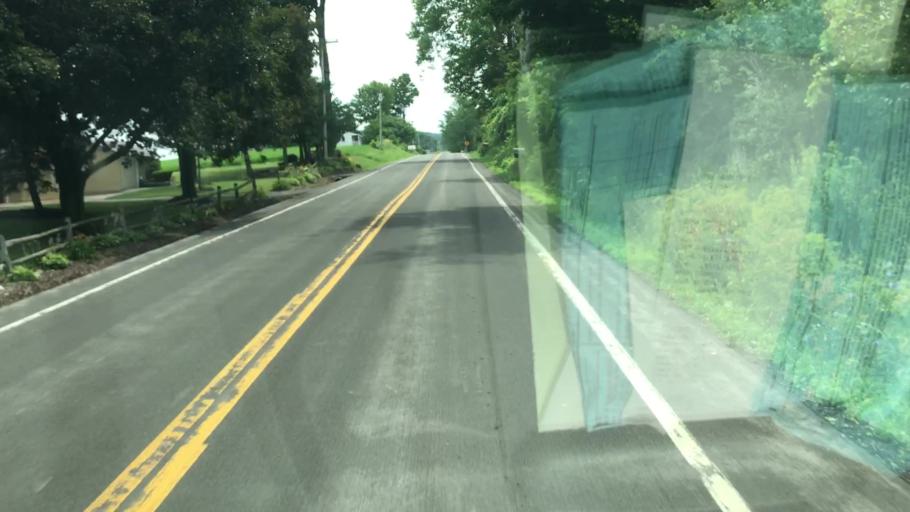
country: US
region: New York
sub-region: Onondaga County
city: Manlius
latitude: 42.9317
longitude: -75.9766
